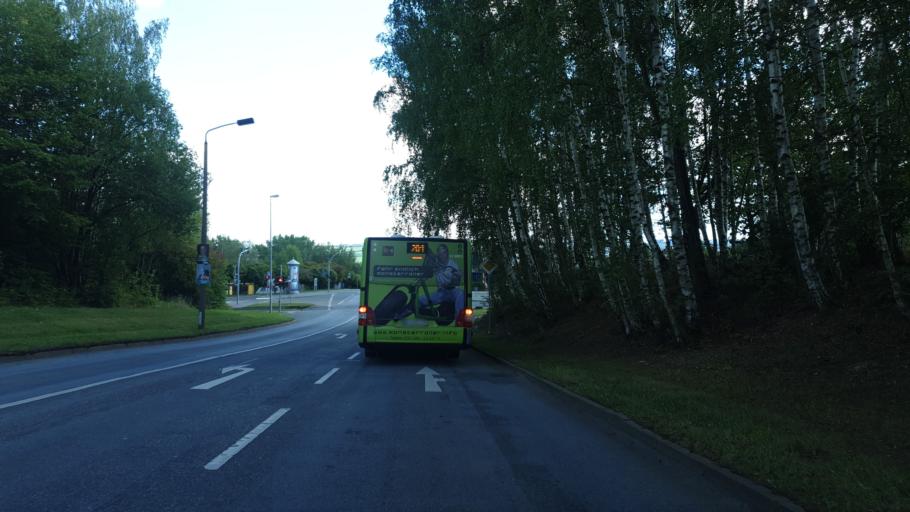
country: DE
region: Saxony
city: Neukirchen
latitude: 50.7843
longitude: 12.8768
